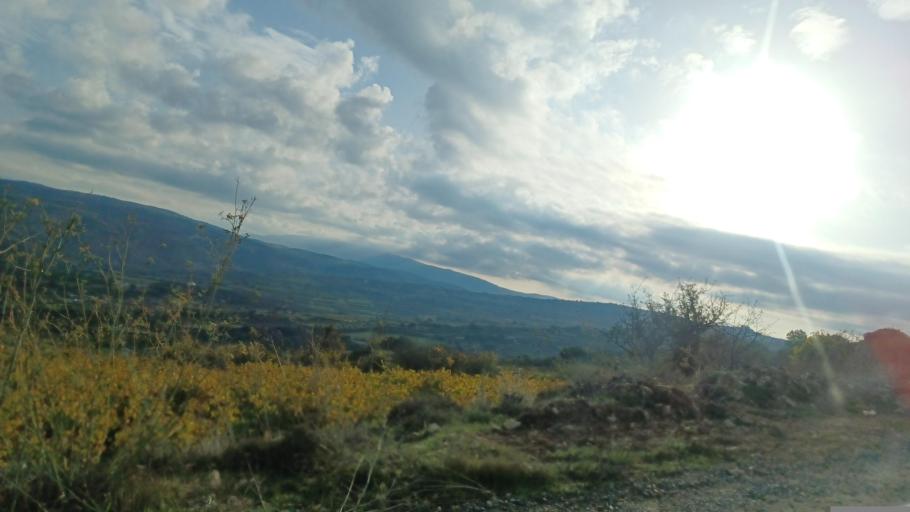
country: CY
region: Pafos
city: Tala
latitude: 34.9079
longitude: 32.4683
